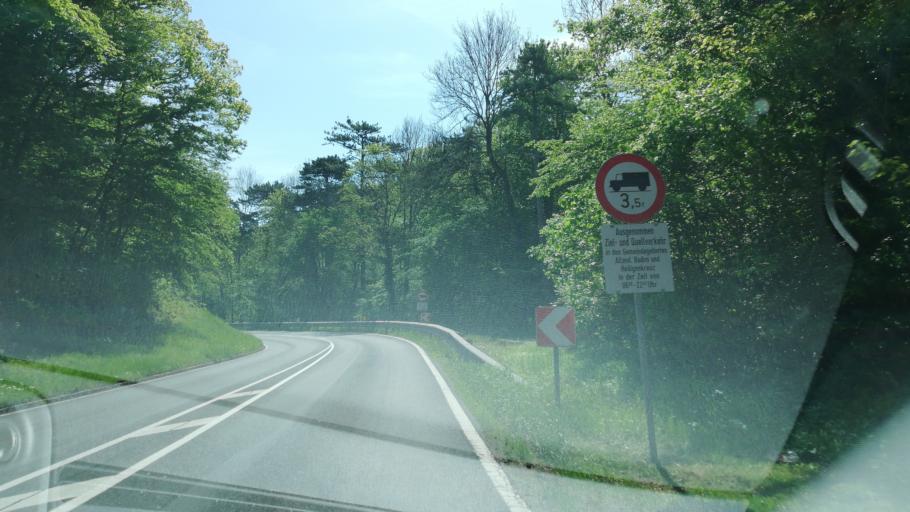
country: AT
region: Lower Austria
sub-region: Politischer Bezirk Modling
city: Gaaden
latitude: 48.0178
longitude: 16.1908
